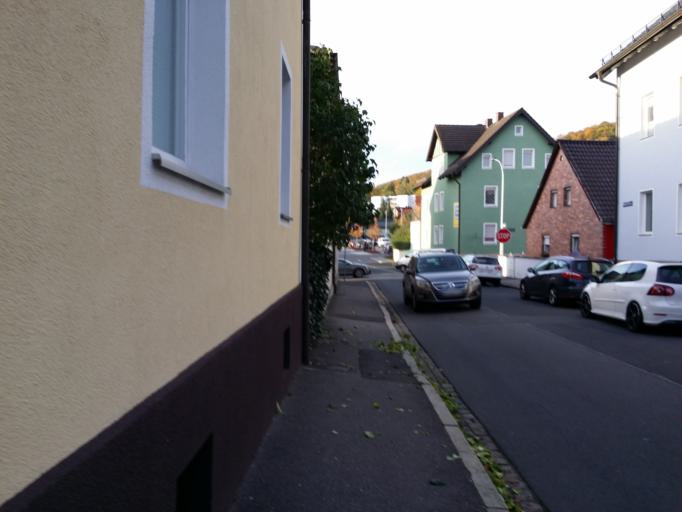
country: DE
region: Bavaria
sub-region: Upper Palatinate
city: Amberg
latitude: 49.4447
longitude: 11.8726
